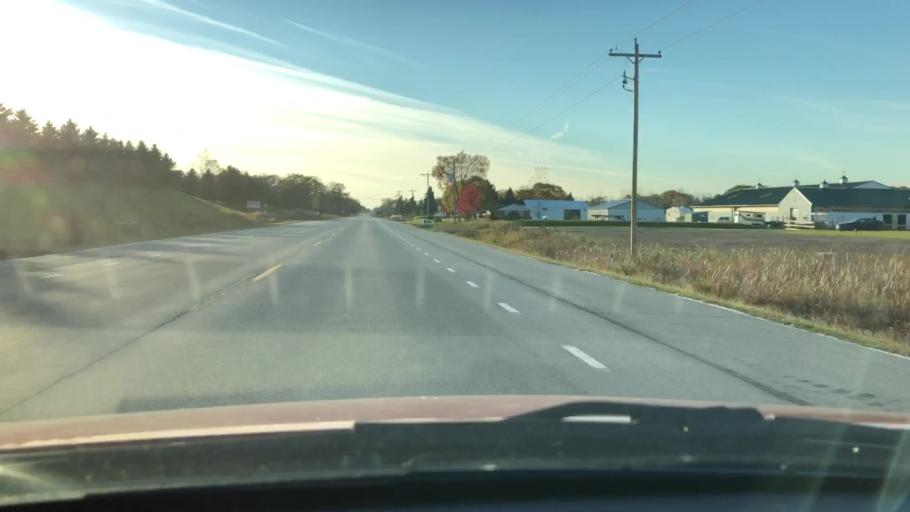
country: US
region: Wisconsin
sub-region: Brown County
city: Oneida
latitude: 44.4442
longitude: -88.1744
